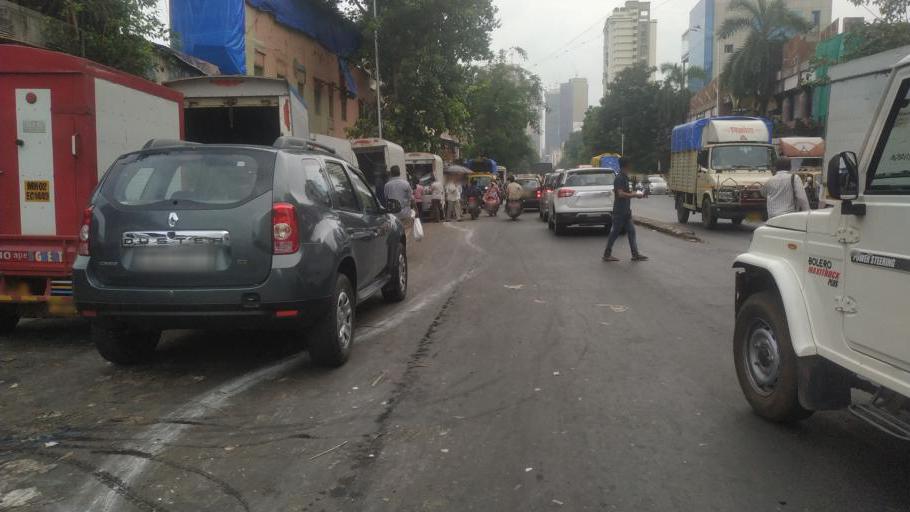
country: IN
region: Maharashtra
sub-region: Mumbai Suburban
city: Mumbai
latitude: 19.0172
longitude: 72.8411
